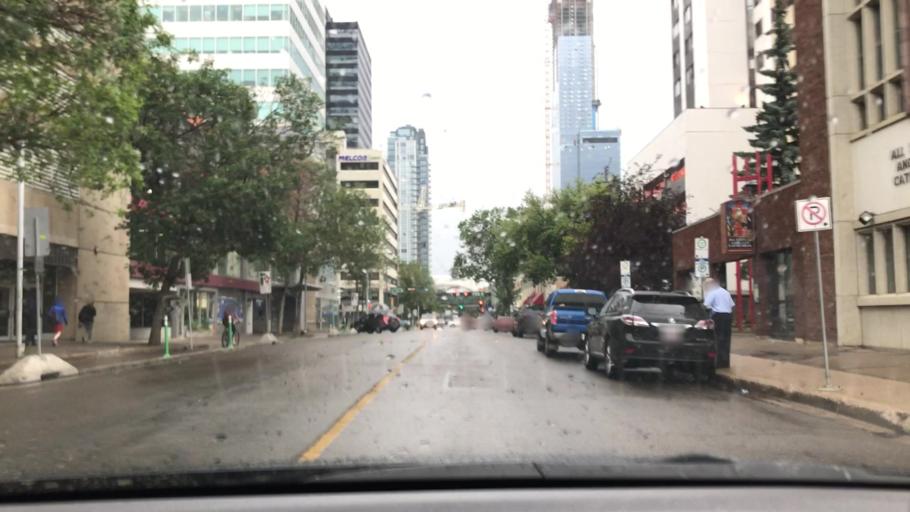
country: CA
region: Alberta
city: Edmonton
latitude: 53.5395
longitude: -113.4974
